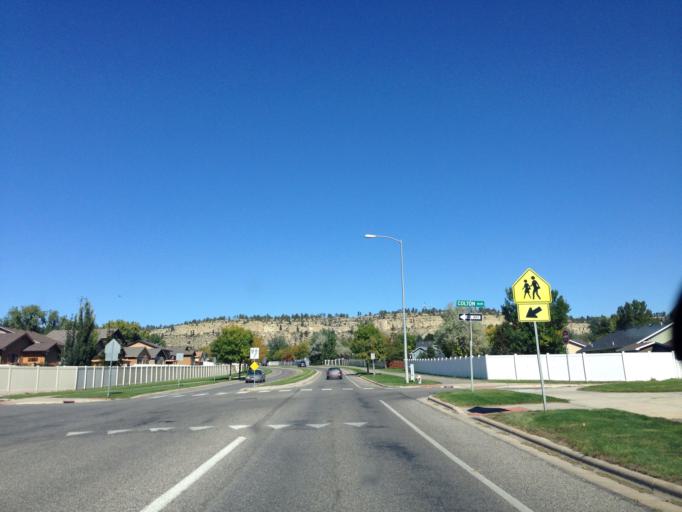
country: US
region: Montana
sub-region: Yellowstone County
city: Billings
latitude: 45.7910
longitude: -108.6008
